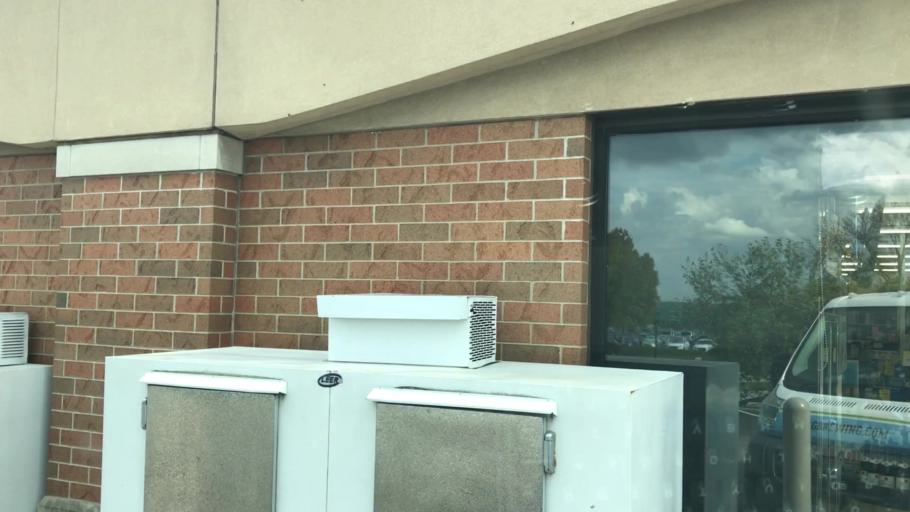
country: US
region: Wisconsin
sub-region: Waukesha County
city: Brookfield
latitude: 43.0373
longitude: -88.1061
